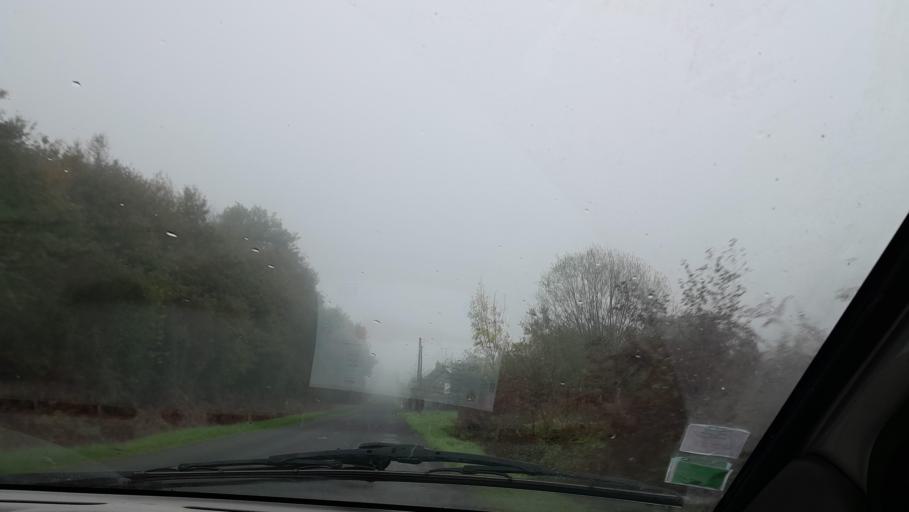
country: FR
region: Pays de la Loire
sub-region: Departement de la Mayenne
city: Saint-Pierre-la-Cour
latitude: 48.0952
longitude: -1.0171
